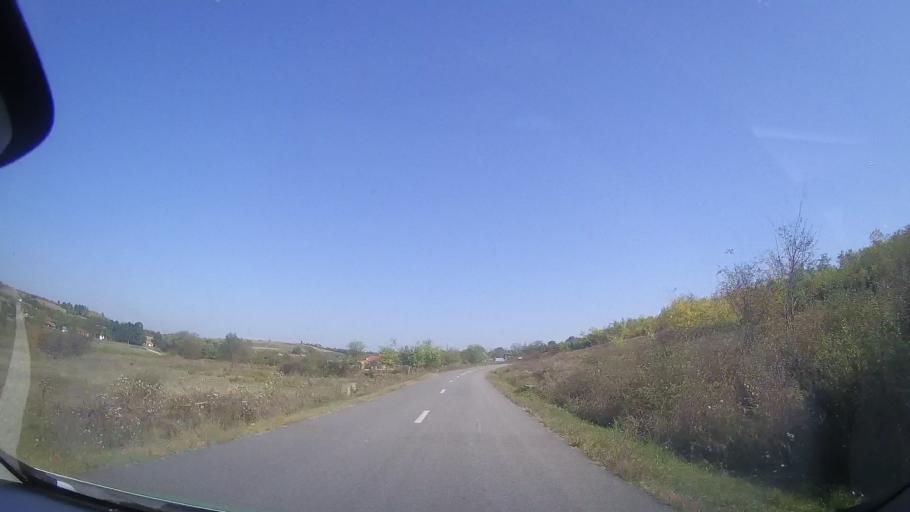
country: RO
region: Timis
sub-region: Comuna Balint
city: Balint
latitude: 45.8396
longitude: 21.8564
